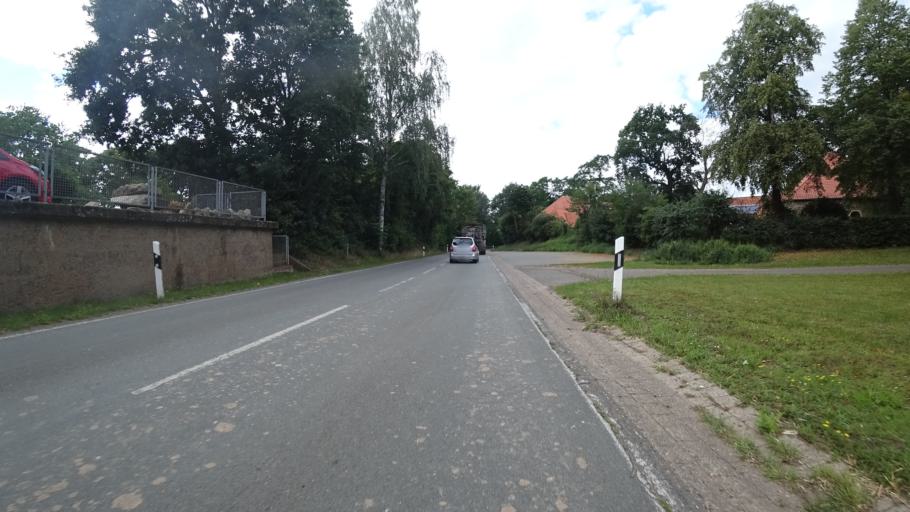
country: DE
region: Lower Saxony
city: Leese
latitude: 52.4789
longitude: 9.0851
